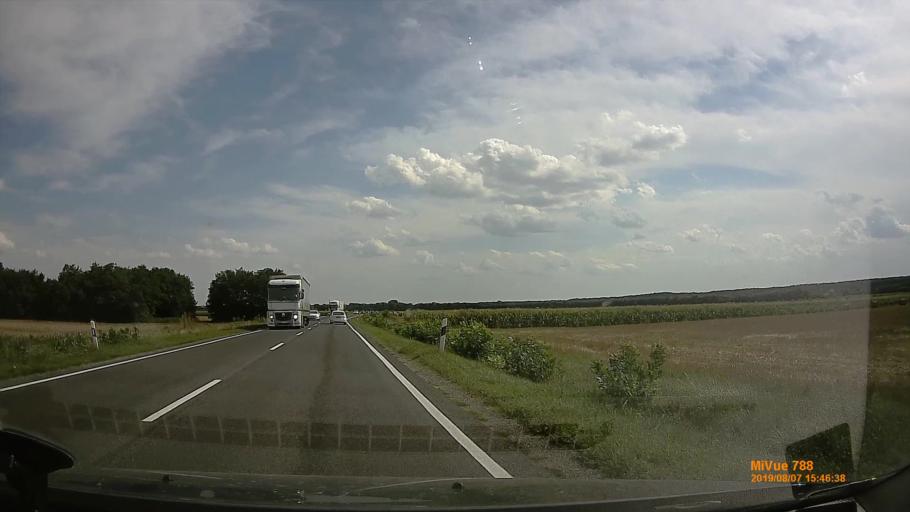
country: HU
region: Vas
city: Szombathely
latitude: 47.1829
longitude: 16.6221
